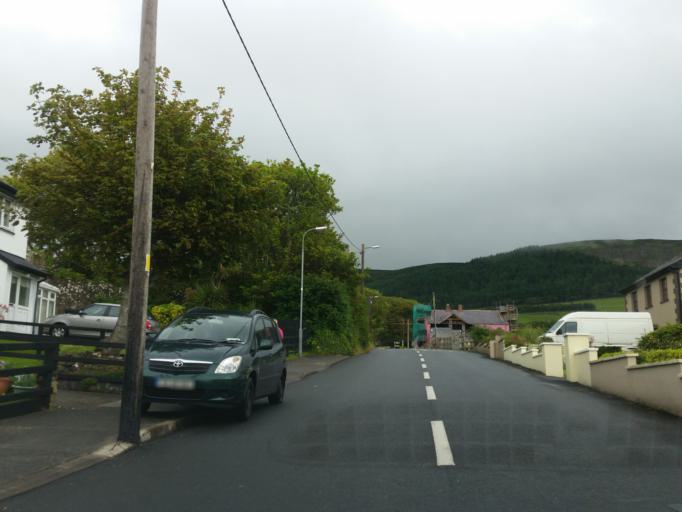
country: IE
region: Connaught
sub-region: Sligo
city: Strandhill
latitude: 54.2681
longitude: -8.5974
